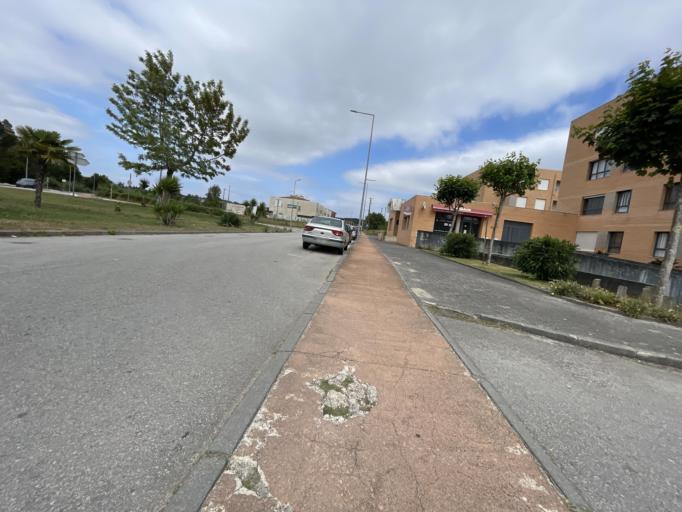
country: PT
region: Aveiro
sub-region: Ovar
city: Cortegaca
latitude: 40.9413
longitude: -8.6353
